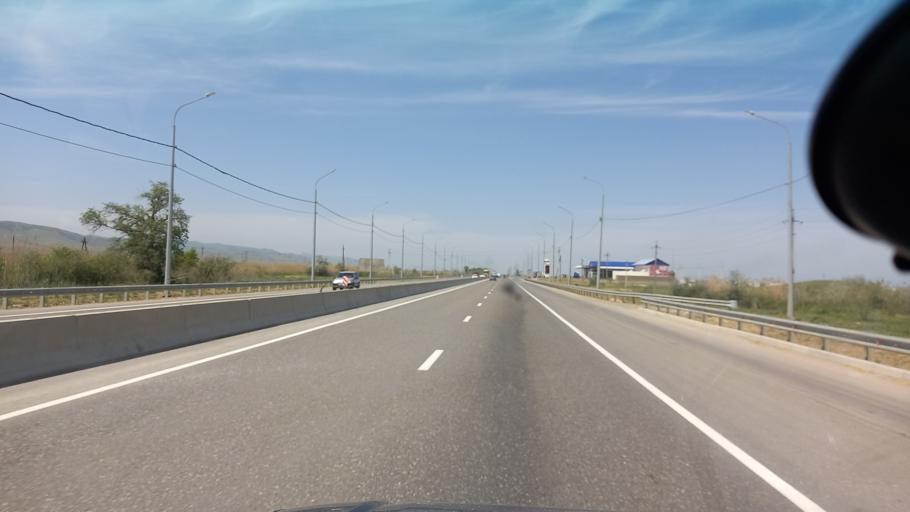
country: RU
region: Dagestan
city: Manas
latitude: 42.7395
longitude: 47.6603
